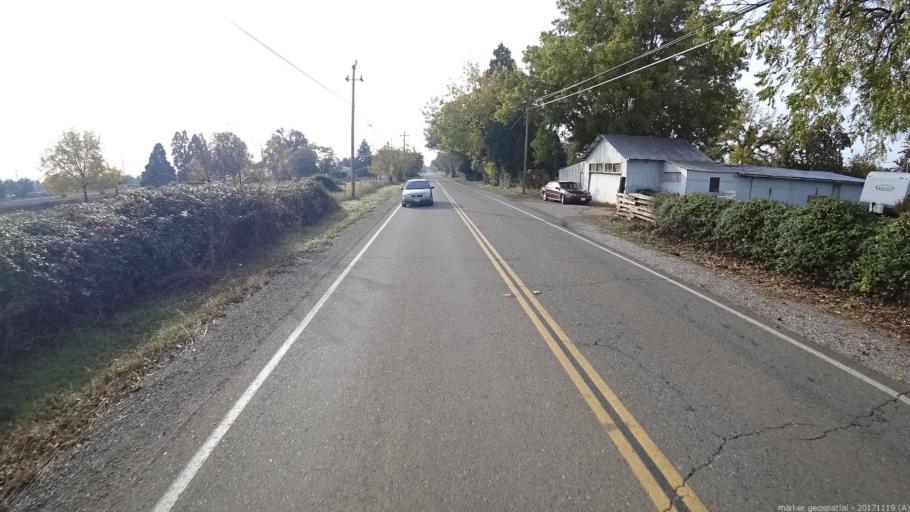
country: US
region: California
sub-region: Shasta County
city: Anderson
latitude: 40.5145
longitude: -122.3336
